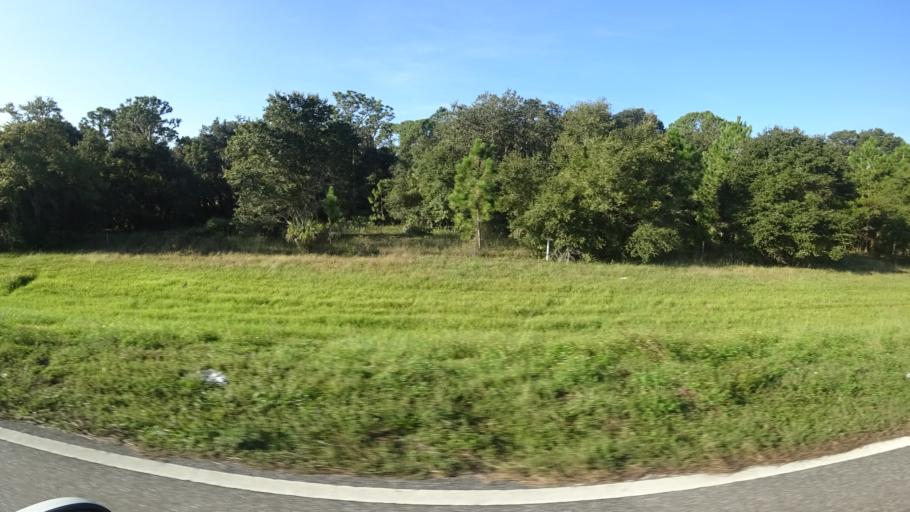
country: US
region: Florida
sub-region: Hillsborough County
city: Sun City Center
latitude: 27.5570
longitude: -82.3672
